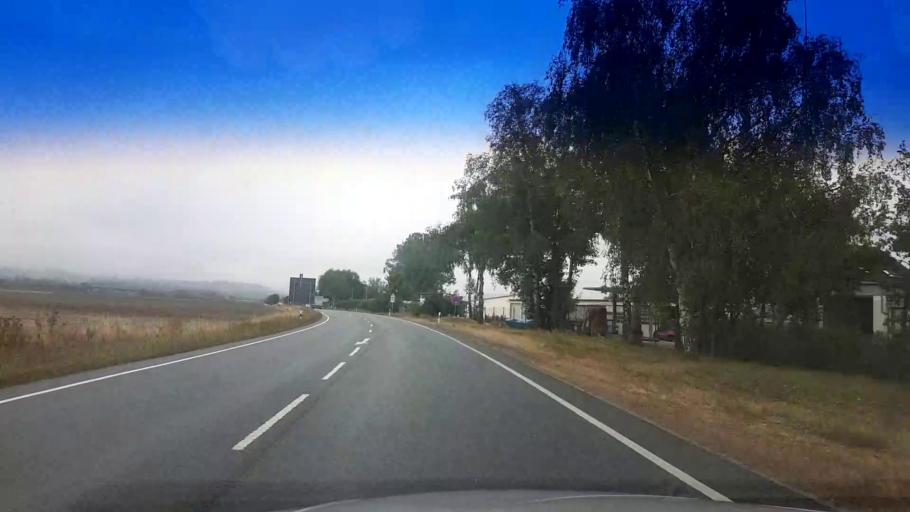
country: DE
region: Bavaria
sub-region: Upper Franconia
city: Eggolsheim
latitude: 49.7690
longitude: 11.0370
